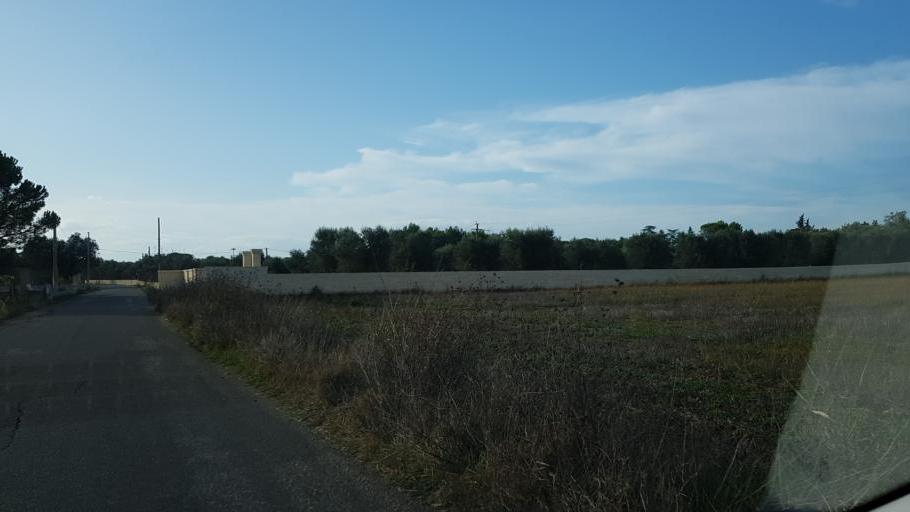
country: IT
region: Apulia
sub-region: Provincia di Brindisi
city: Oria
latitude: 40.5090
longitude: 17.6650
